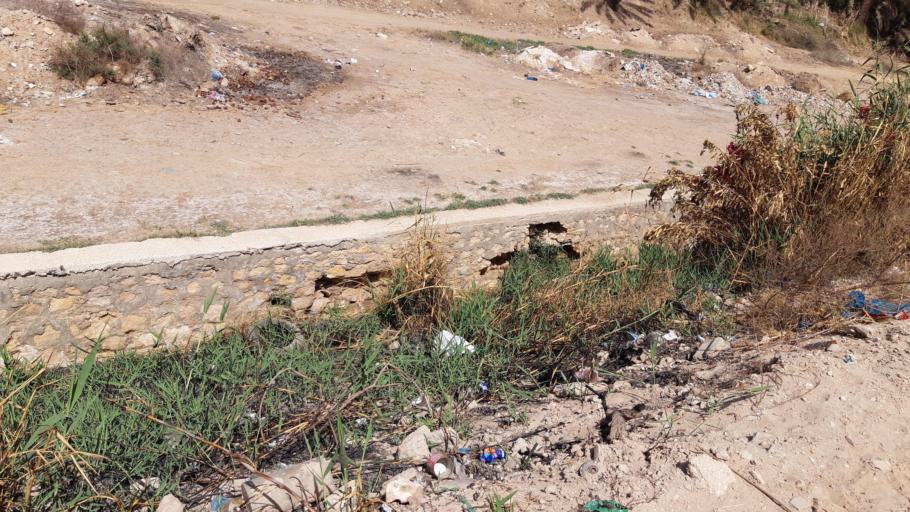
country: TN
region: Qabis
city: Gabes
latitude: 33.8747
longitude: 10.0892
